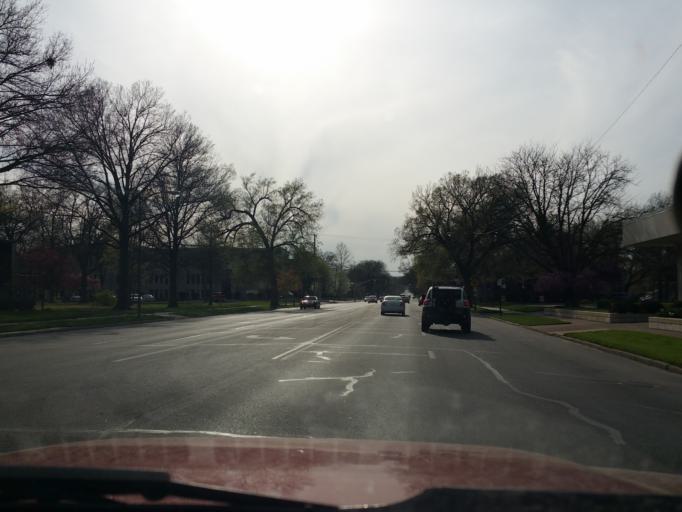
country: US
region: Kansas
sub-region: Riley County
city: Manhattan
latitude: 39.1795
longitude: -96.5684
